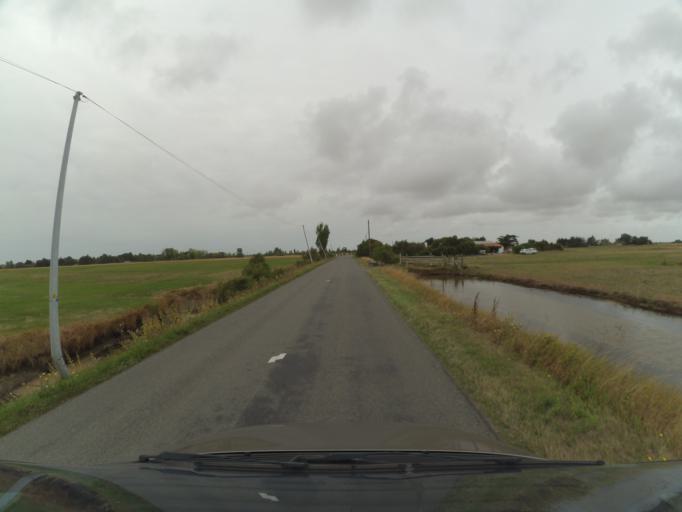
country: FR
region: Pays de la Loire
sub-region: Departement de la Vendee
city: Beauvoir-sur-Mer
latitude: 46.8747
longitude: -2.0516
